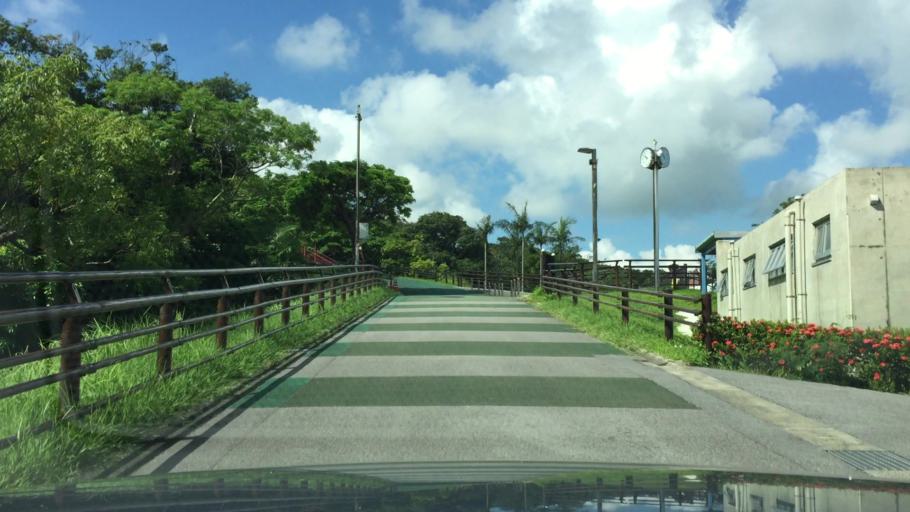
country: JP
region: Okinawa
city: Ishigaki
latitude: 24.3855
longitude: 124.1606
